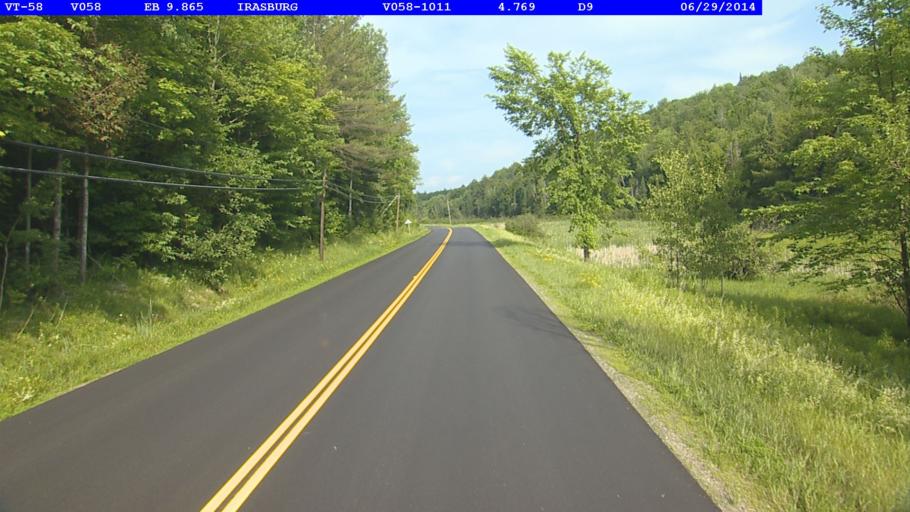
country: US
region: Vermont
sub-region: Orleans County
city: Newport
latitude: 44.8043
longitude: -72.2500
